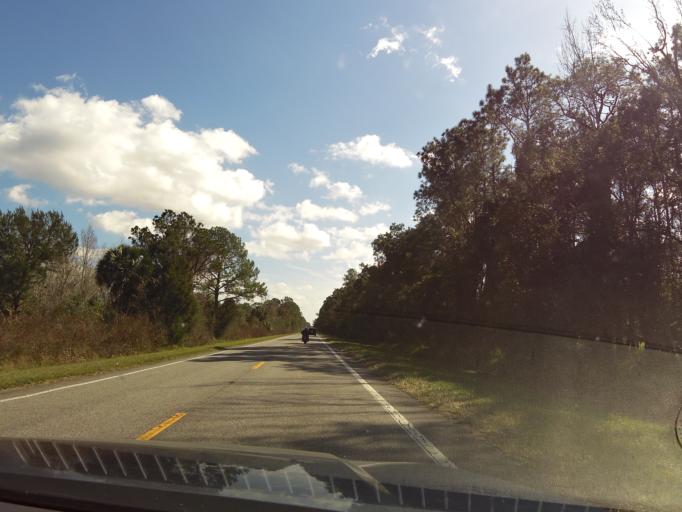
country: US
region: Florida
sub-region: Volusia County
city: De Leon Springs
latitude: 29.1582
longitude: -81.3841
